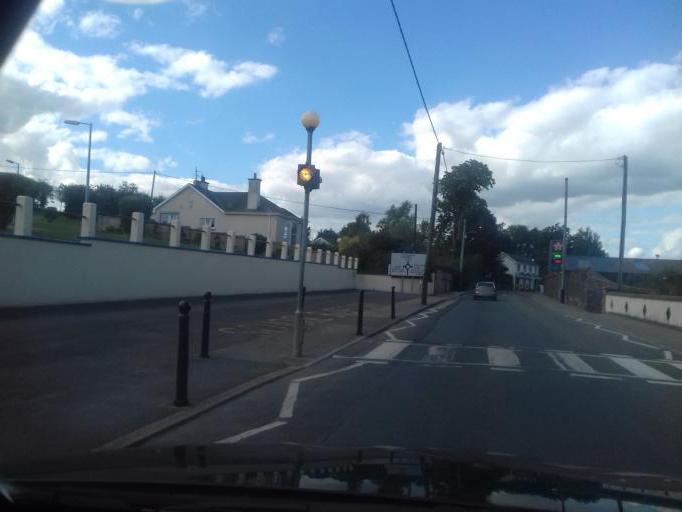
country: IE
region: Leinster
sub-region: Kilkenny
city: Thomastown
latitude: 52.5284
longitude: -7.1420
